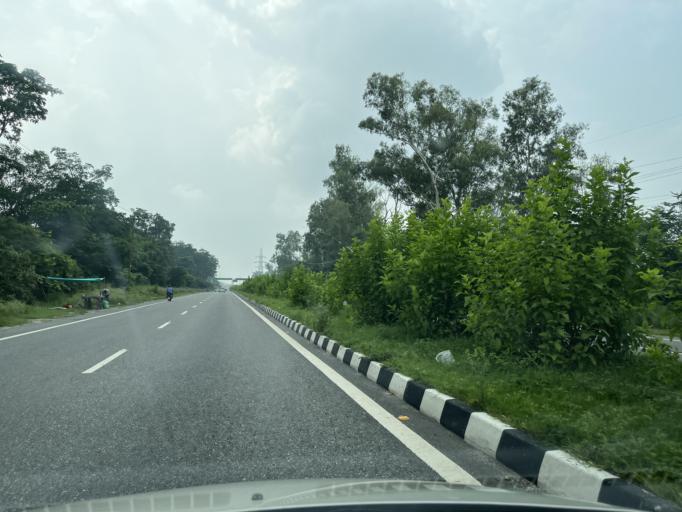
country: IN
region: Uttarakhand
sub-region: Dehradun
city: Doiwala
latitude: 30.1084
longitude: 78.1721
